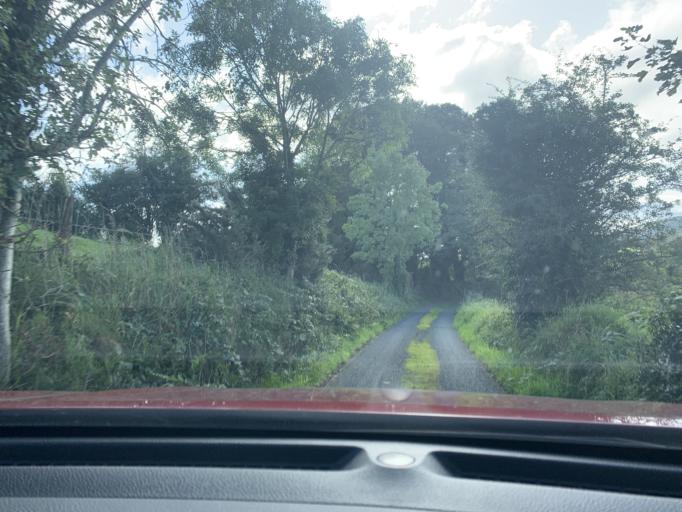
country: IE
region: Connaught
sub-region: Roscommon
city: Boyle
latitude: 54.0762
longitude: -8.3640
